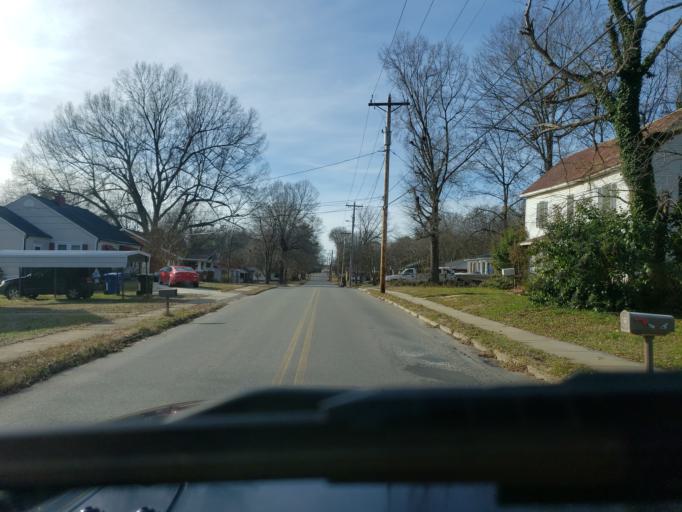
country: US
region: North Carolina
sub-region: Cleveland County
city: Kings Mountain
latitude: 35.2382
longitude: -81.3551
